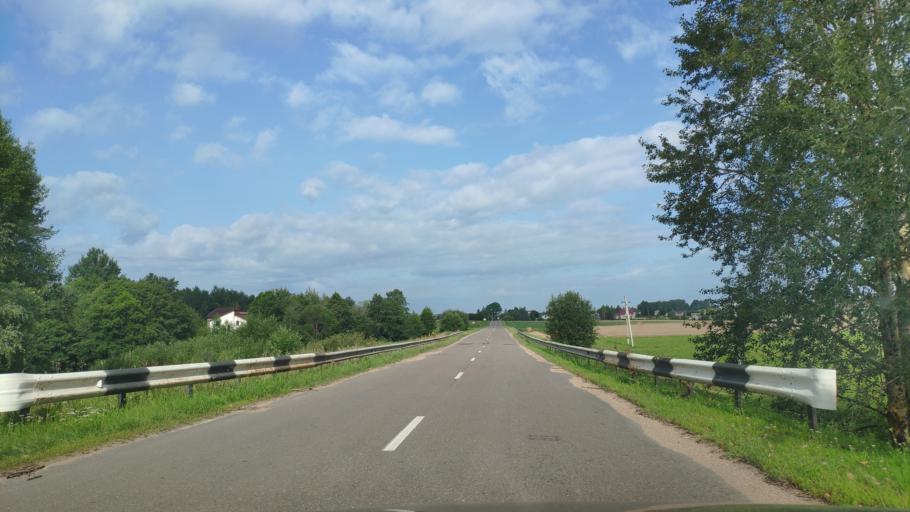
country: BY
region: Minsk
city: Khatsyezhyna
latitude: 53.8790
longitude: 27.2851
